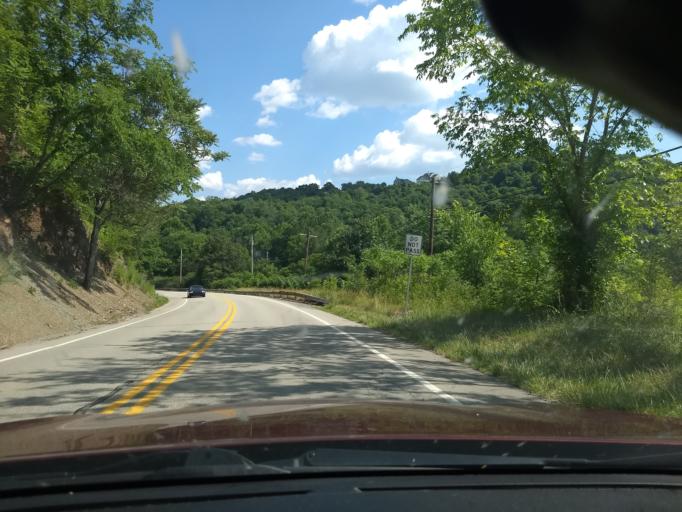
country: US
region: Pennsylvania
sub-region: Westmoreland County
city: Trafford
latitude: 40.3736
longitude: -79.7610
